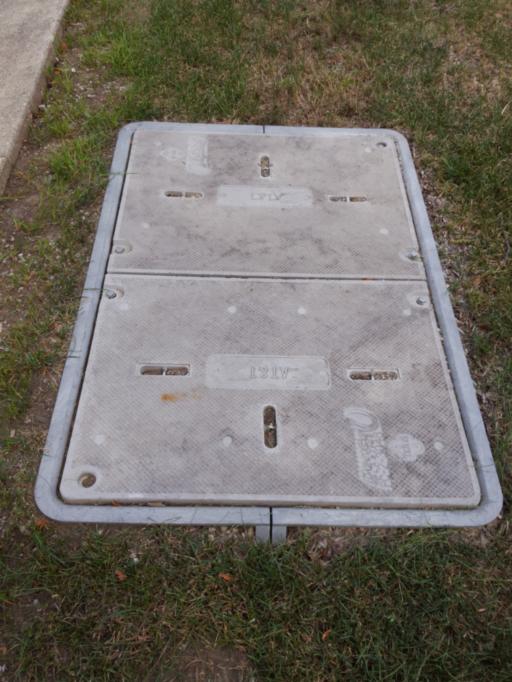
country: US
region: Illinois
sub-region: Lake County
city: Deerfield
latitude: 42.1648
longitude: -87.8460
